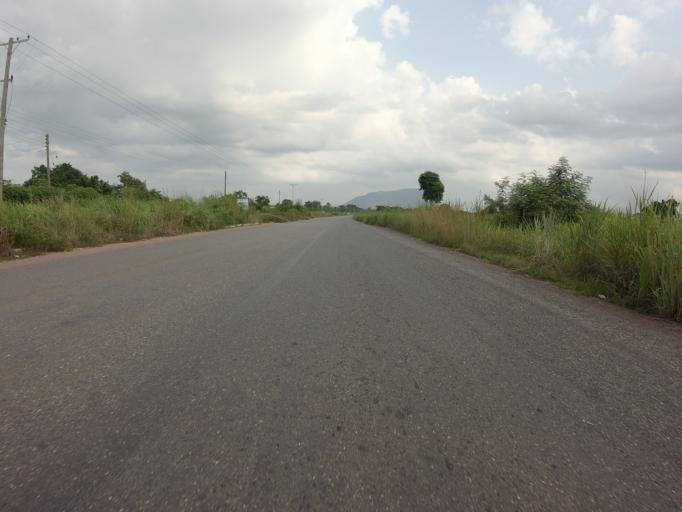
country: GH
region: Volta
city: Ho
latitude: 6.5728
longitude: 0.4846
